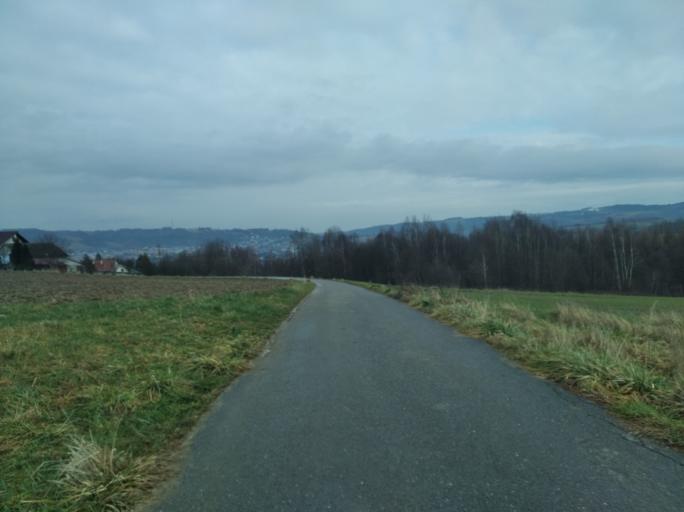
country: PL
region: Subcarpathian Voivodeship
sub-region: Powiat strzyzowski
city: Strzyzow
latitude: 49.8538
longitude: 21.7812
